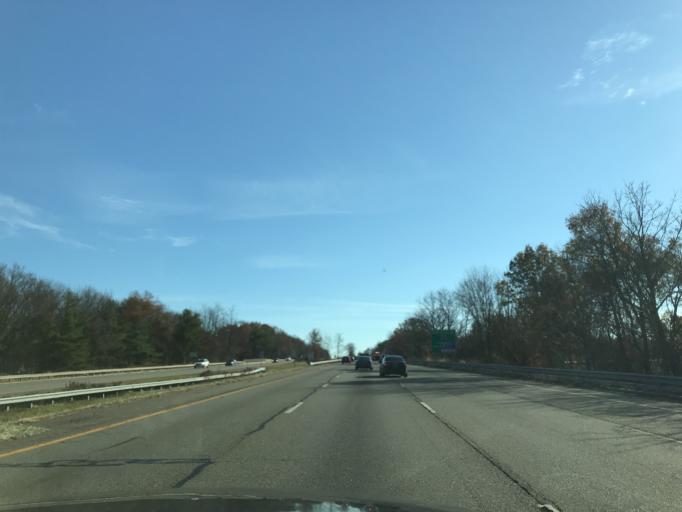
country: US
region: New Jersey
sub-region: Essex County
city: West Caldwell
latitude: 40.8226
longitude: -74.3184
